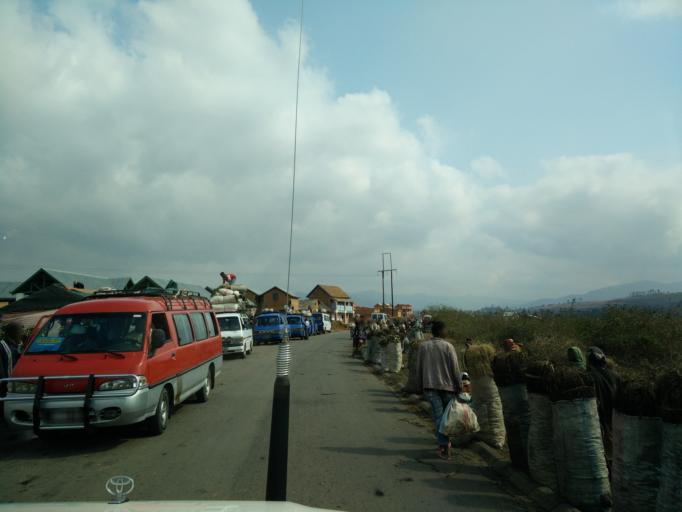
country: MG
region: Upper Matsiatra
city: Fianarantsoa
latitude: -21.3773
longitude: 47.1686
